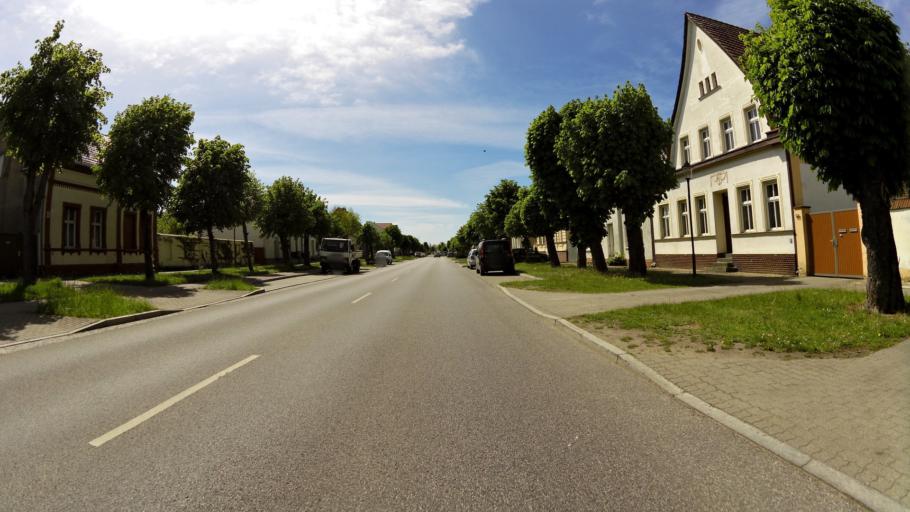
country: DE
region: Brandenburg
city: Wandlitz
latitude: 52.6761
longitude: 13.4393
